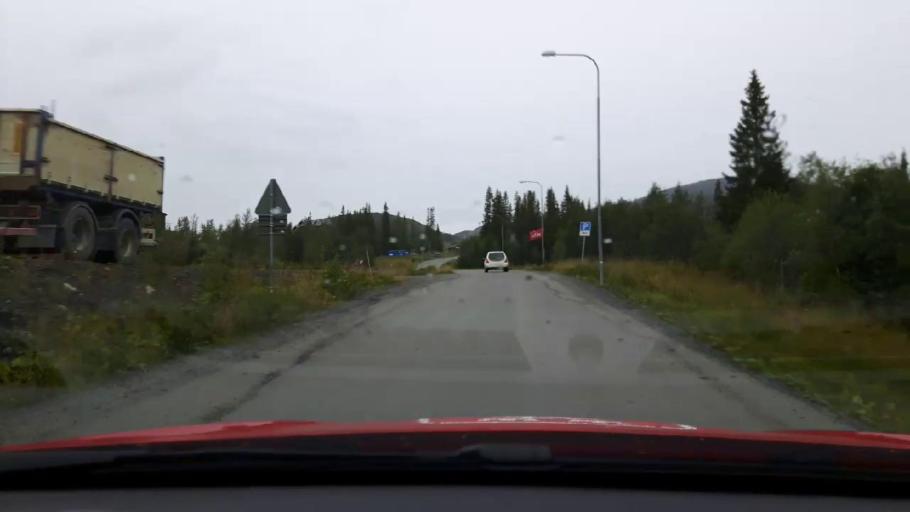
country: SE
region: Jaemtland
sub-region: Are Kommun
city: Are
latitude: 63.3907
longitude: 13.1509
